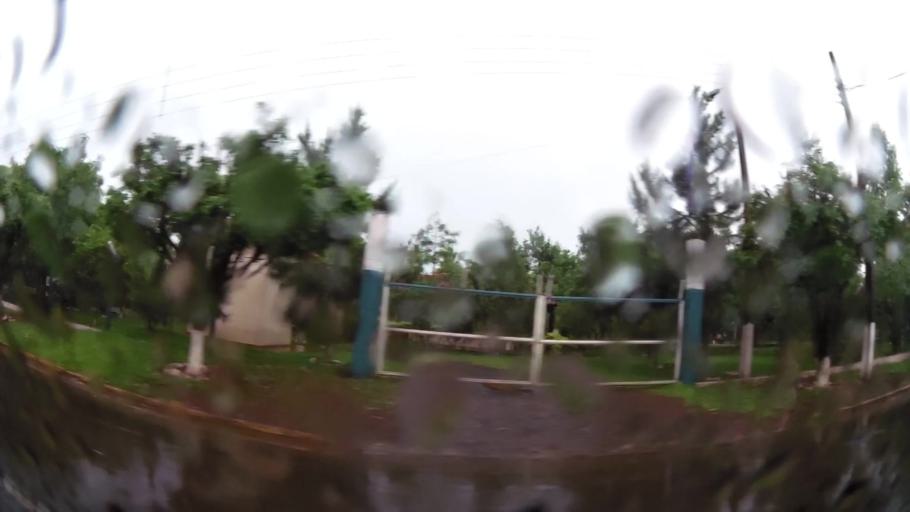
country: PY
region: Alto Parana
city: Presidente Franco
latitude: -25.5328
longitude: -54.6807
